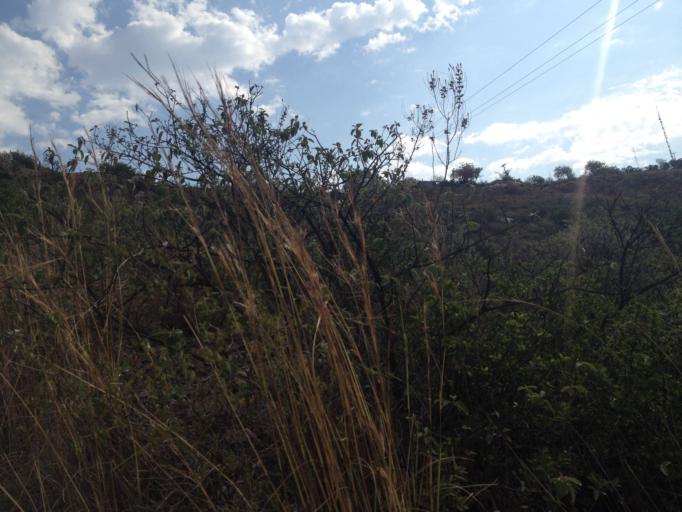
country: MX
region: Nuevo Leon
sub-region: Monterrey
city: Monterrey
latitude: 25.6535
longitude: -100.3315
